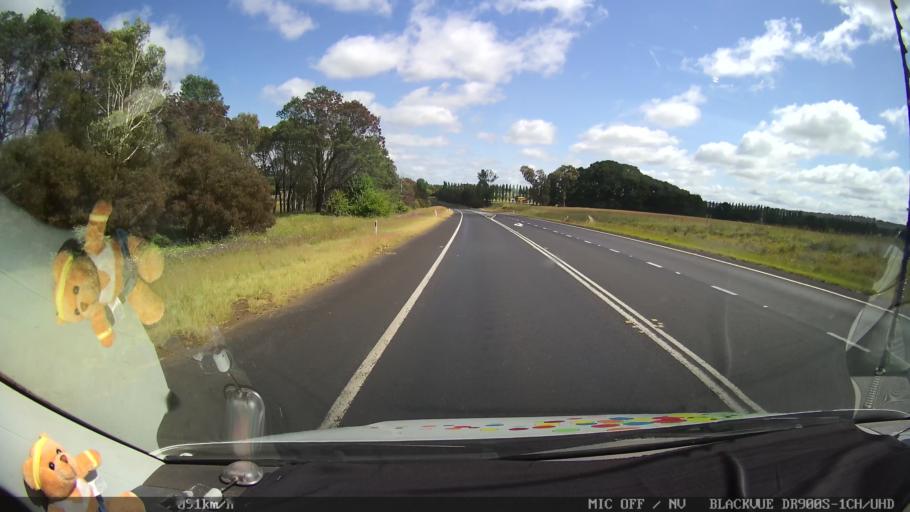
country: AU
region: New South Wales
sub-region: Glen Innes Severn
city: Glen Innes
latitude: -29.8620
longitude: 151.7378
